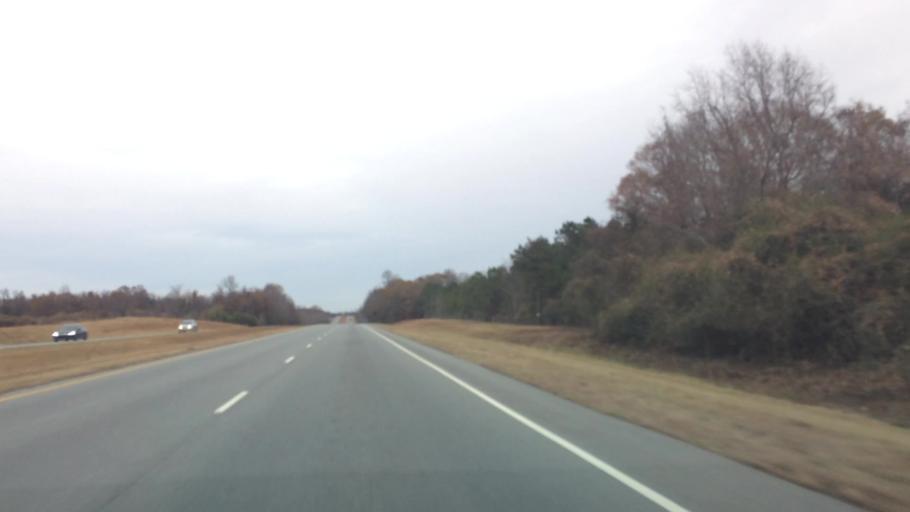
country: US
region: North Carolina
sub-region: Wayne County
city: Mount Olive
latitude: 35.1409
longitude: -78.1323
